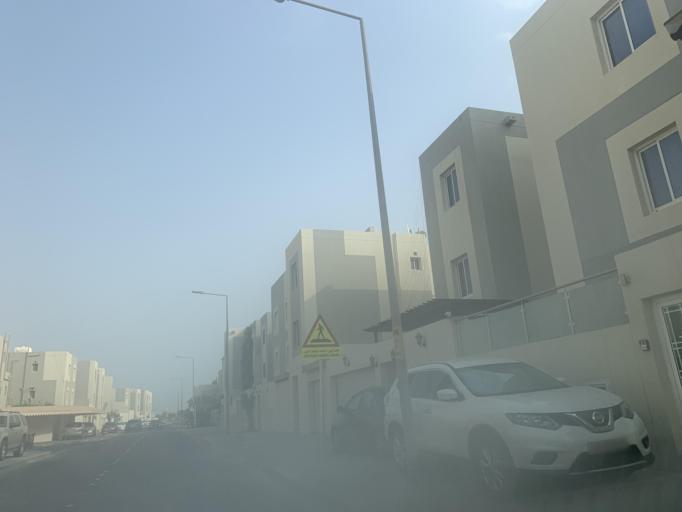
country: BH
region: Manama
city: Jidd Hafs
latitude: 26.2271
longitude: 50.4543
